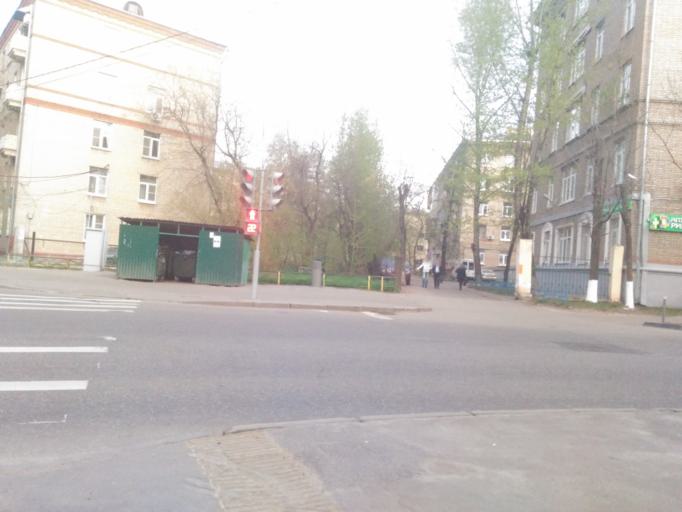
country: RU
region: Moskovskaya
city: Khoroshevo-Mnevniki
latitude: 55.7919
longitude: 37.4831
